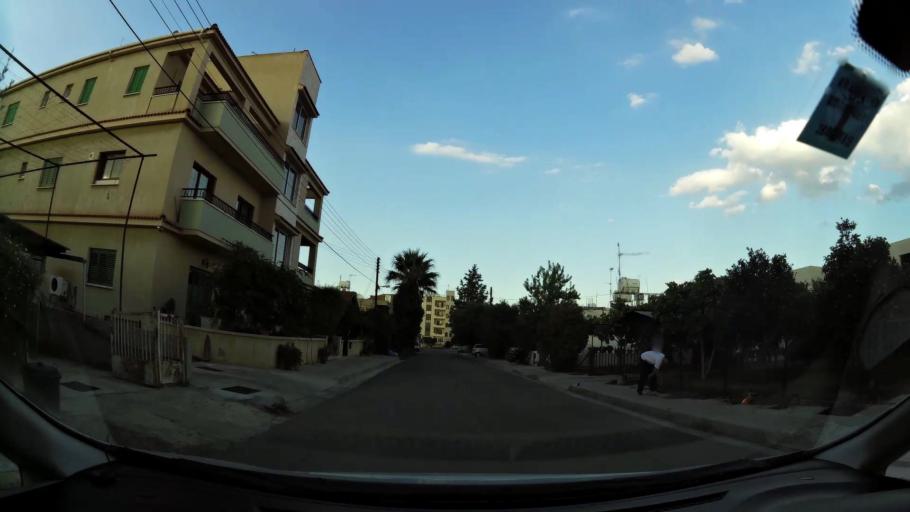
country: CY
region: Lefkosia
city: Tseri
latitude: 35.1271
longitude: 33.3286
